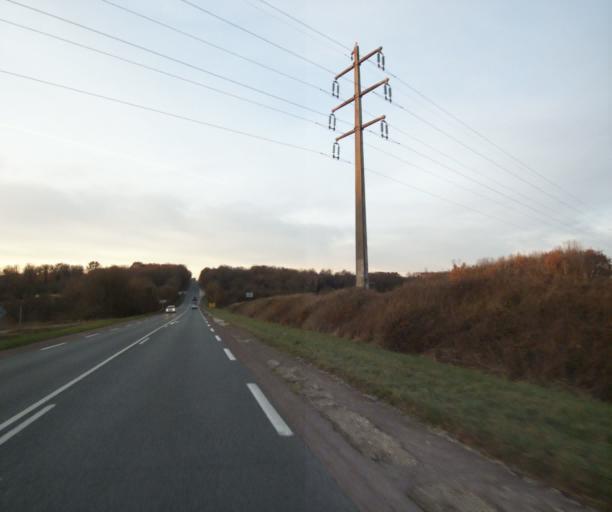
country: FR
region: Poitou-Charentes
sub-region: Departement de la Charente-Maritime
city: Saintes
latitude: 45.7584
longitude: -0.6631
